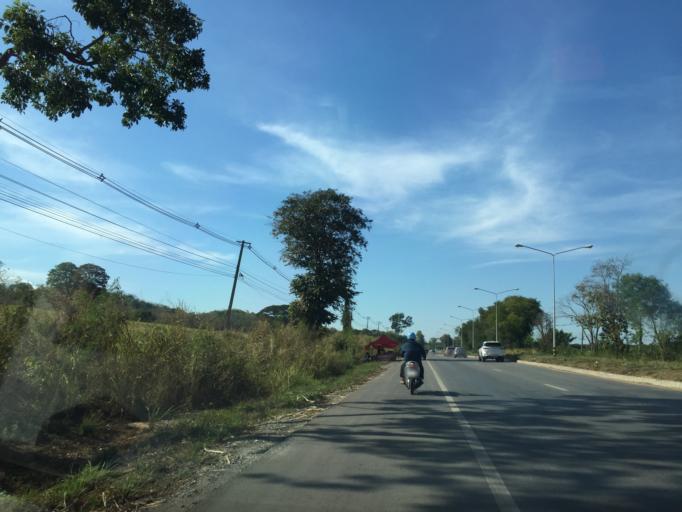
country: TH
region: Loei
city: Wang Saphung
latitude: 17.2952
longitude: 101.8167
